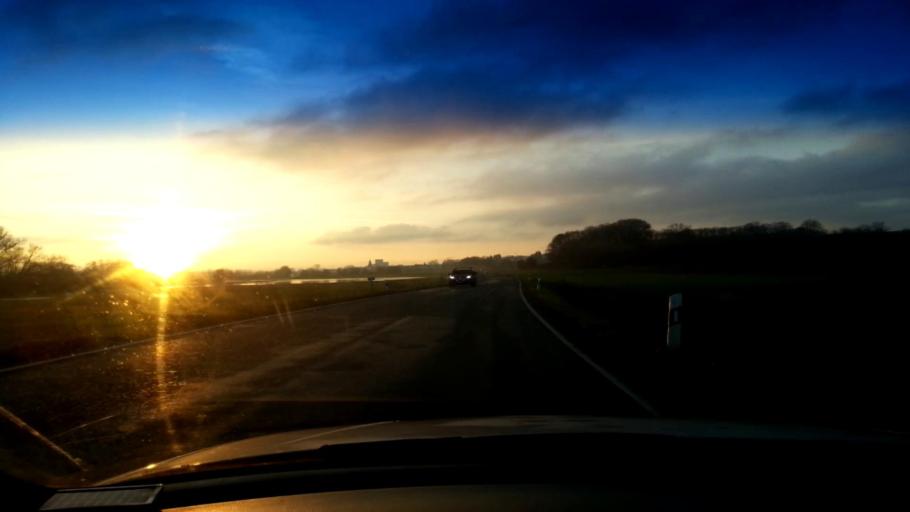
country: DE
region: Bavaria
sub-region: Upper Franconia
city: Frensdorf
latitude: 49.7862
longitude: 10.8606
